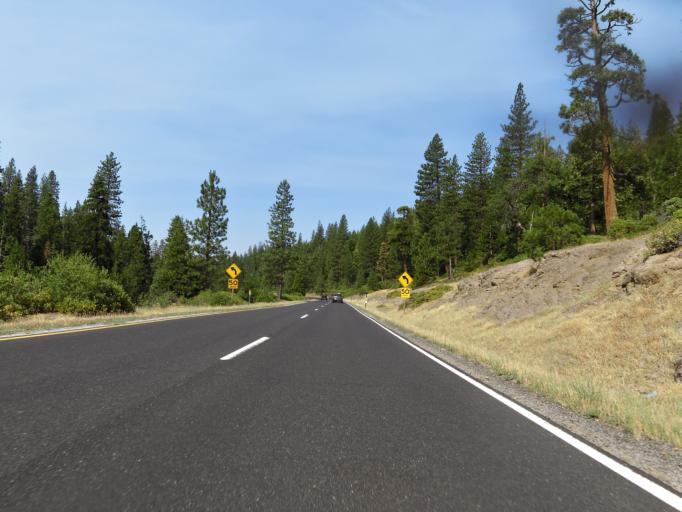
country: US
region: California
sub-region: Tuolumne County
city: Twain Harte
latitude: 38.1249
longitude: -120.1087
